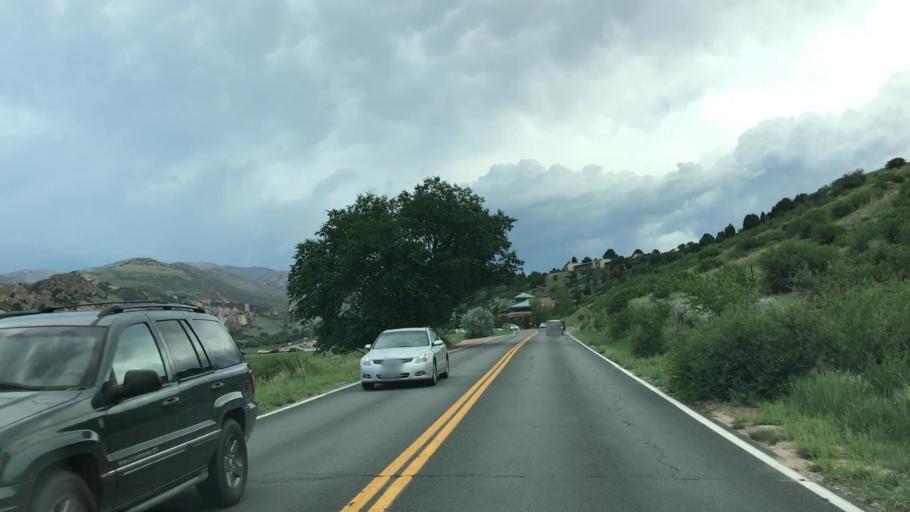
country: US
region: Colorado
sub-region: El Paso County
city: Manitou Springs
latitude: 38.8746
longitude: -104.8691
